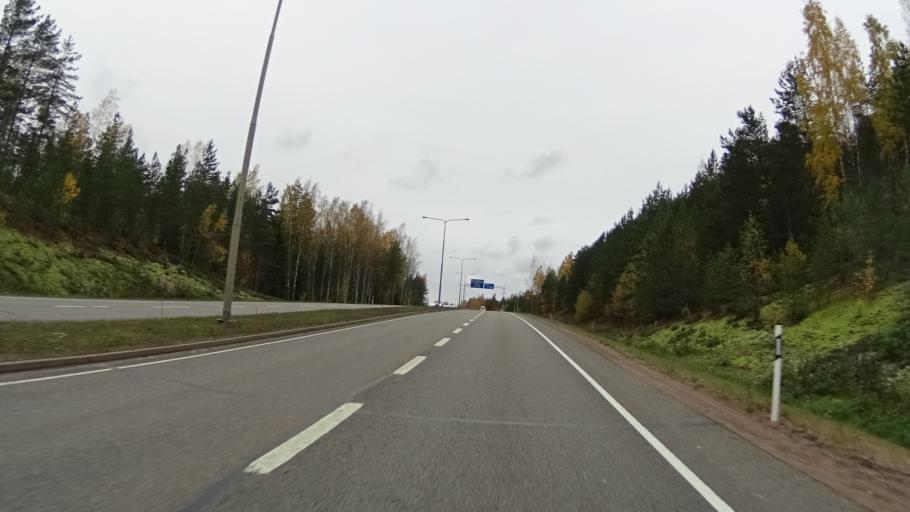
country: FI
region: Kymenlaakso
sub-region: Kouvola
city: Kouvola
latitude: 60.8796
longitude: 26.7780
